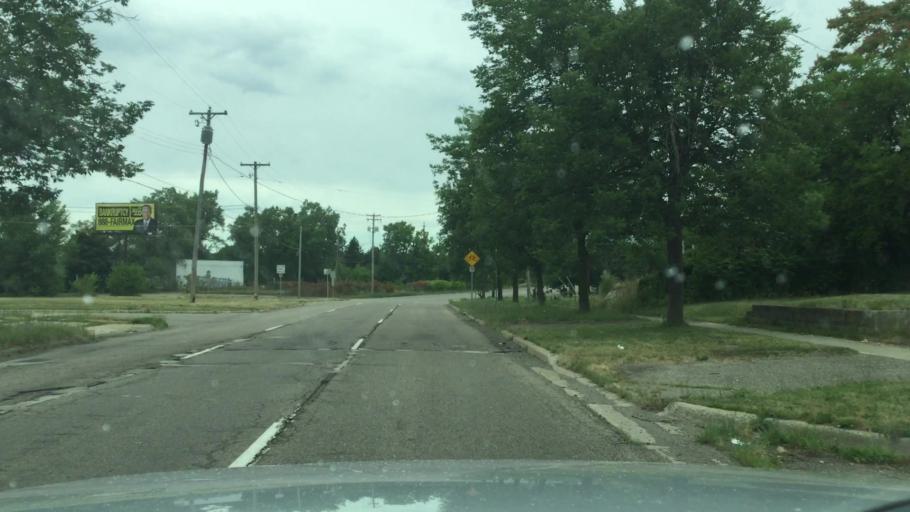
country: US
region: Michigan
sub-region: Genesee County
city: Flint
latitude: 43.0341
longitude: -83.6796
